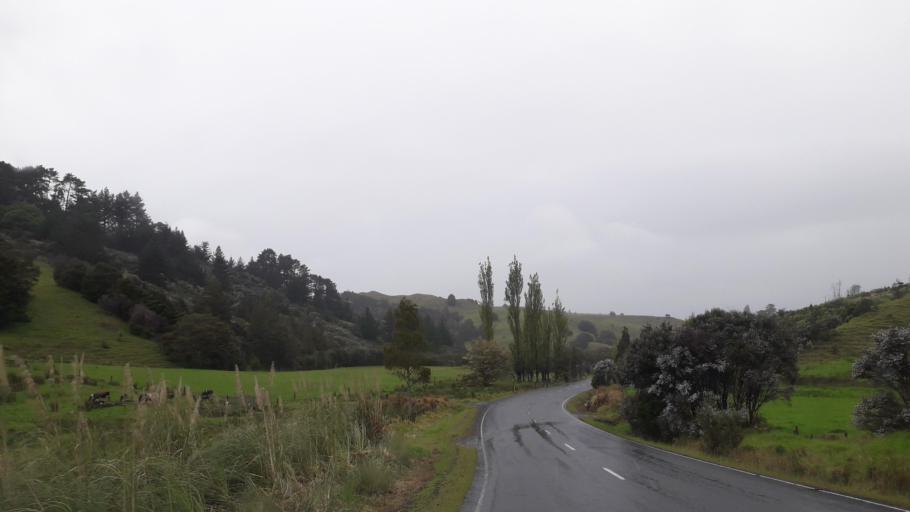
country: NZ
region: Northland
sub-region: Far North District
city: Kaitaia
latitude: -35.3596
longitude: 173.4683
